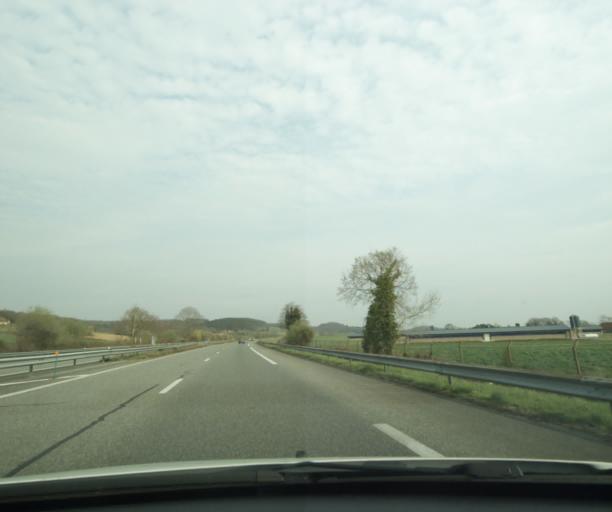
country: FR
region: Aquitaine
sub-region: Departement des Pyrenees-Atlantiques
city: Denguin
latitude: 43.3850
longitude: -0.5174
